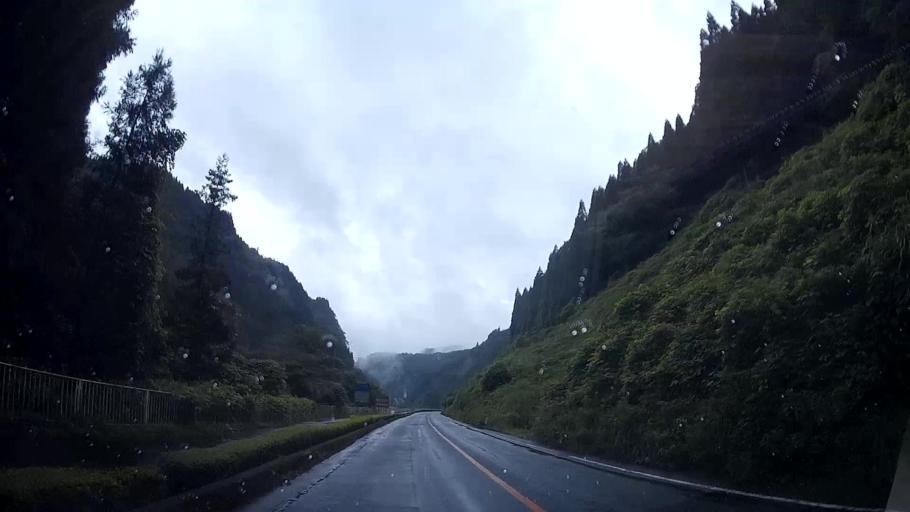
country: JP
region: Oita
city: Tsukawaki
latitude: 33.1782
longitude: 131.0363
